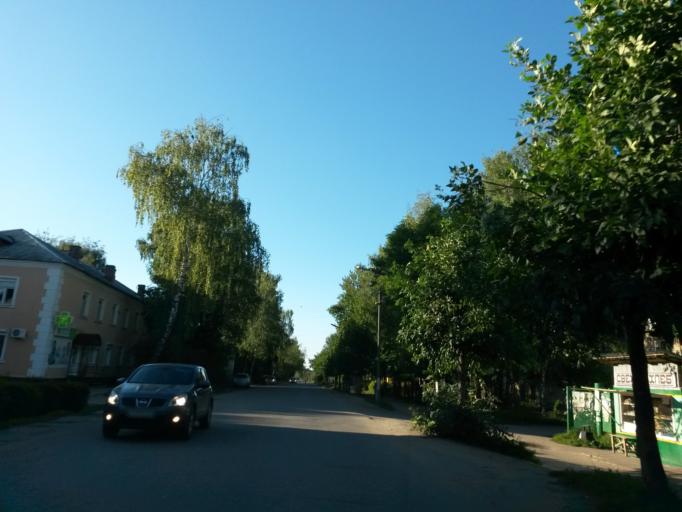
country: RU
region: Jaroslavl
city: Gavrilov-Yam
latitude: 57.3037
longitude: 39.8622
